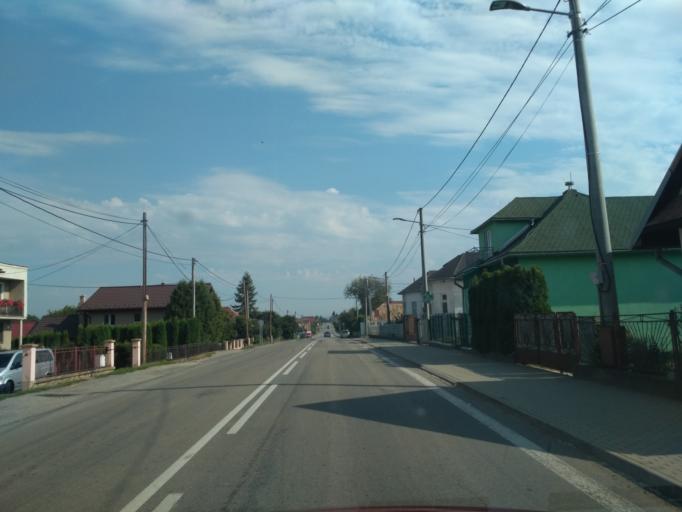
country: SK
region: Kosicky
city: Kosice
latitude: 48.8501
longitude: 21.2729
